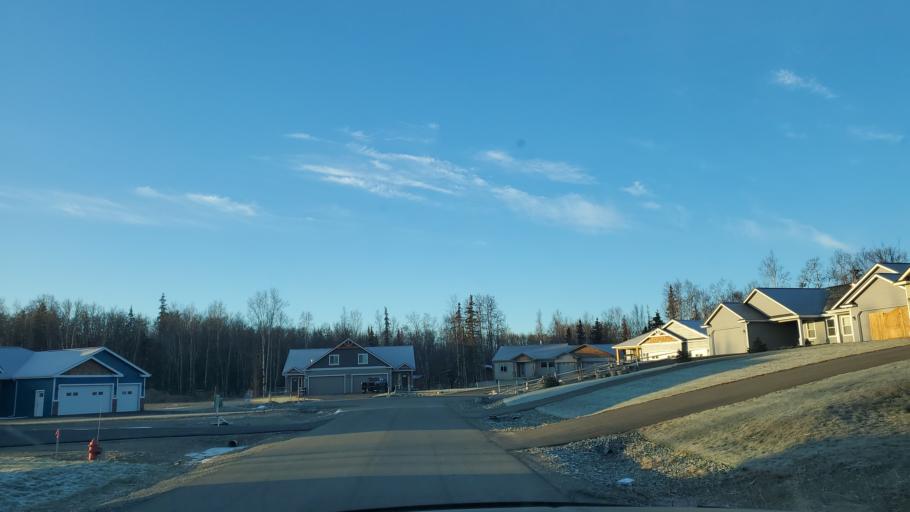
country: US
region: Alaska
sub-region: Matanuska-Susitna Borough
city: Wasilla
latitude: 61.5903
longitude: -149.4557
